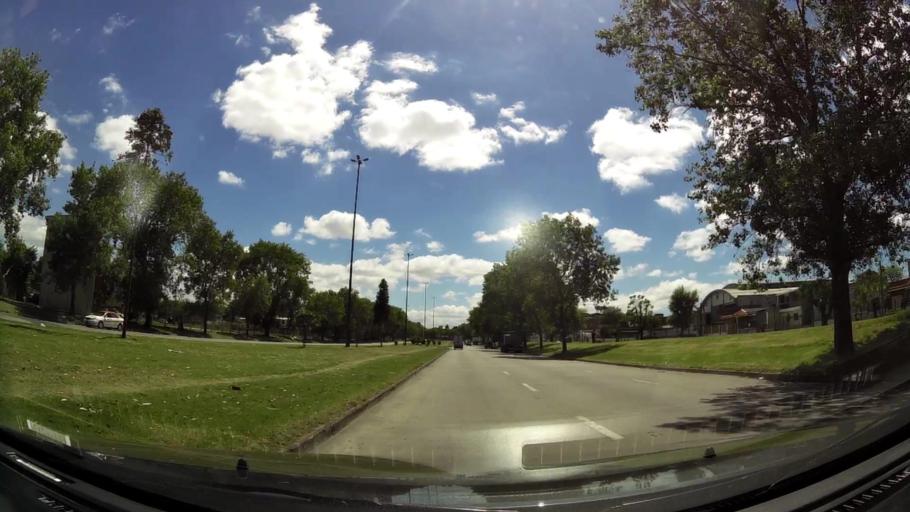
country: UY
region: Montevideo
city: Montevideo
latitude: -34.8600
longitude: -56.1455
